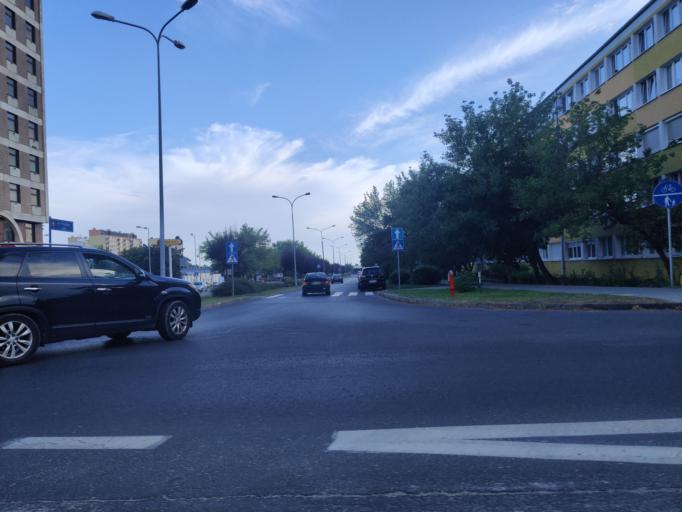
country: PL
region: Greater Poland Voivodeship
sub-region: Konin
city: Konin
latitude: 52.2299
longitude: 18.2720
